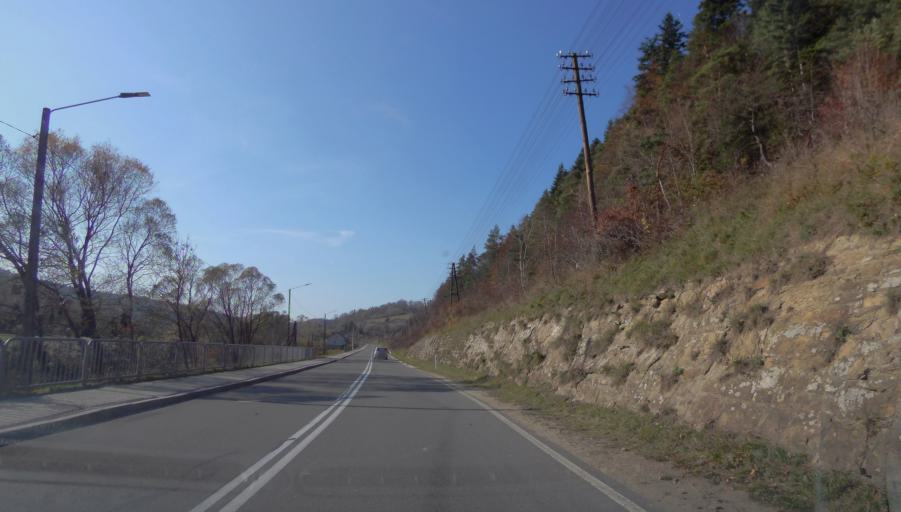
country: PL
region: Subcarpathian Voivodeship
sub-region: Powiat sanocki
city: Komancza
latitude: 49.3457
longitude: 22.0800
